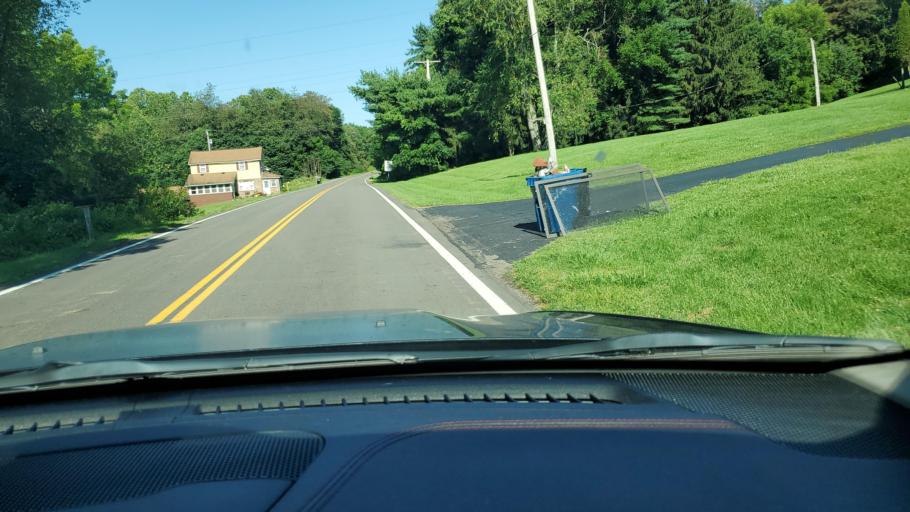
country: US
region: Ohio
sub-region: Mahoning County
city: Lowellville
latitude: 41.0329
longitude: -80.5203
